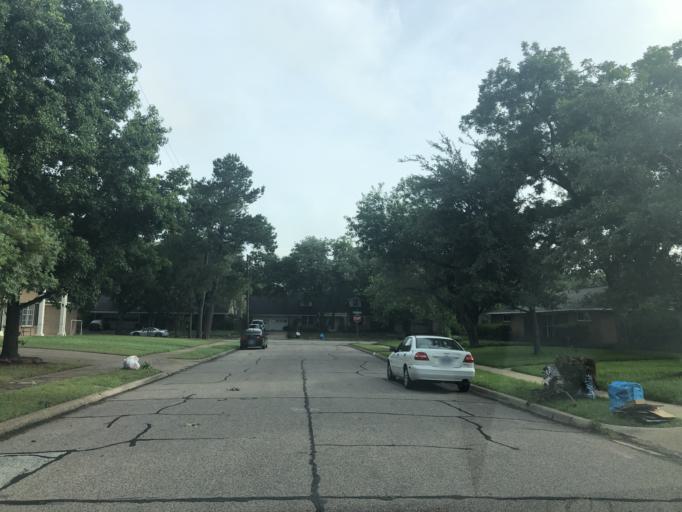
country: US
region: Texas
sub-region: Dallas County
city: Irving
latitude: 32.8039
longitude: -96.9842
